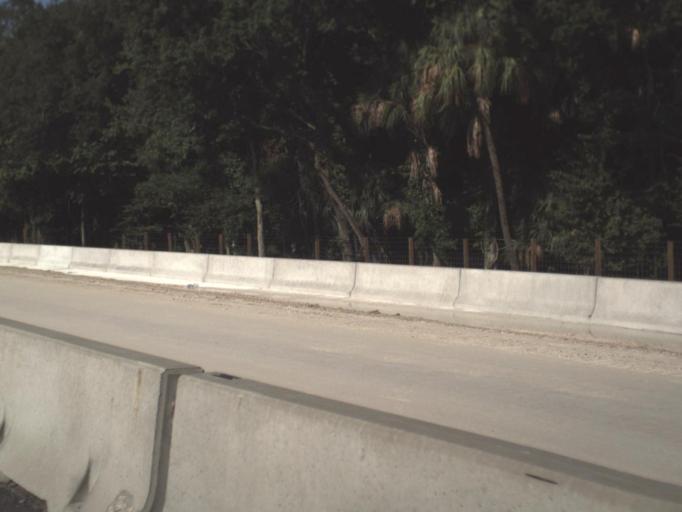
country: US
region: Florida
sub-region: Hillsborough County
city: Pebble Creek
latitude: 28.1805
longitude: -82.3901
